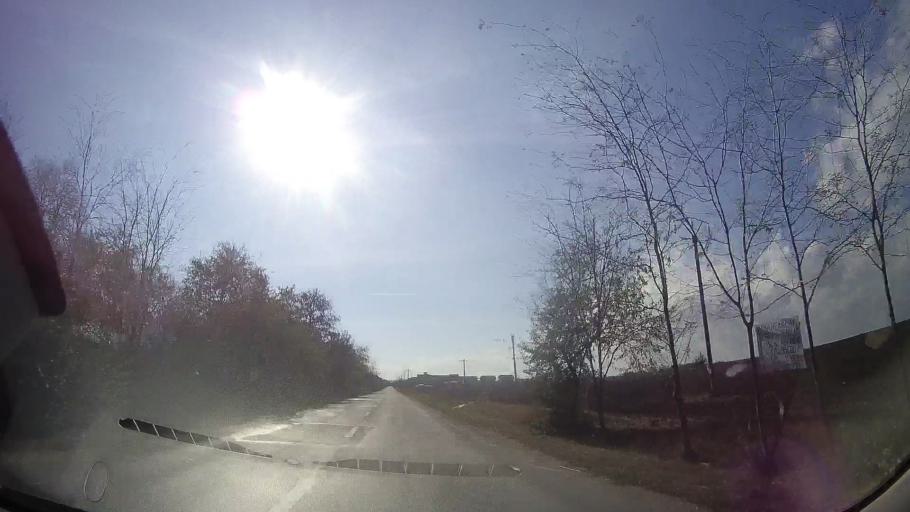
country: RO
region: Constanta
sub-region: Comuna Costinesti
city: Costinesti
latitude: 43.9603
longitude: 28.6359
